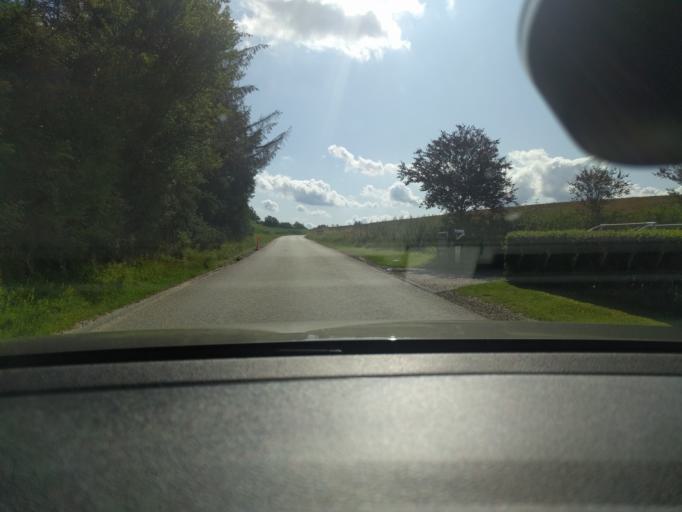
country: DK
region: Central Jutland
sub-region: Viborg Kommune
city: Viborg
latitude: 56.5242
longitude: 9.3771
